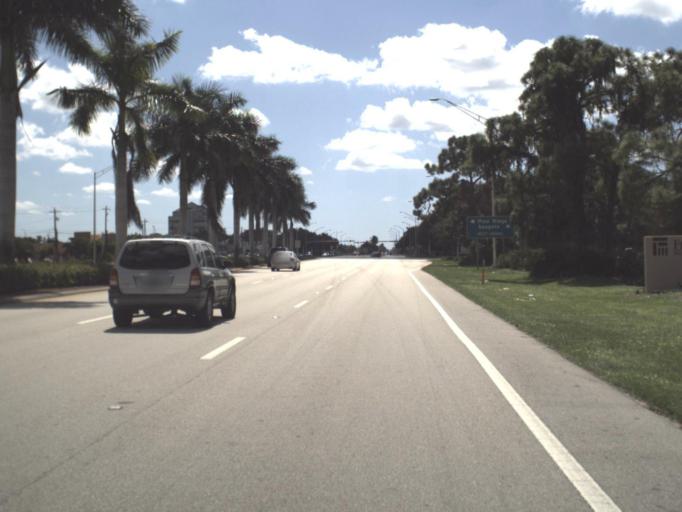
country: US
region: Florida
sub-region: Collier County
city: Pine Ridge
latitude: 26.2152
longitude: -81.8006
